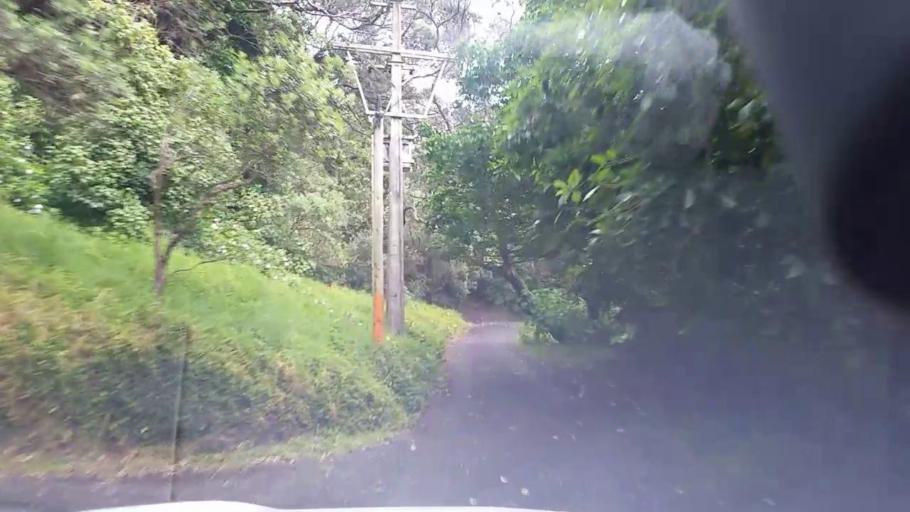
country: NZ
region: Auckland
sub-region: Auckland
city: Muriwai Beach
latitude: -36.9855
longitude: 174.4779
